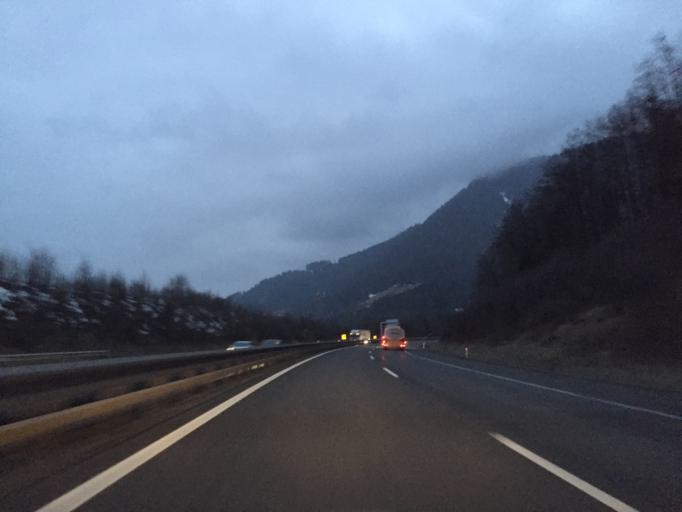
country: AT
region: Salzburg
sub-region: Politischer Bezirk Sankt Johann im Pongau
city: Eben im Pongau
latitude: 47.4241
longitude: 13.3565
